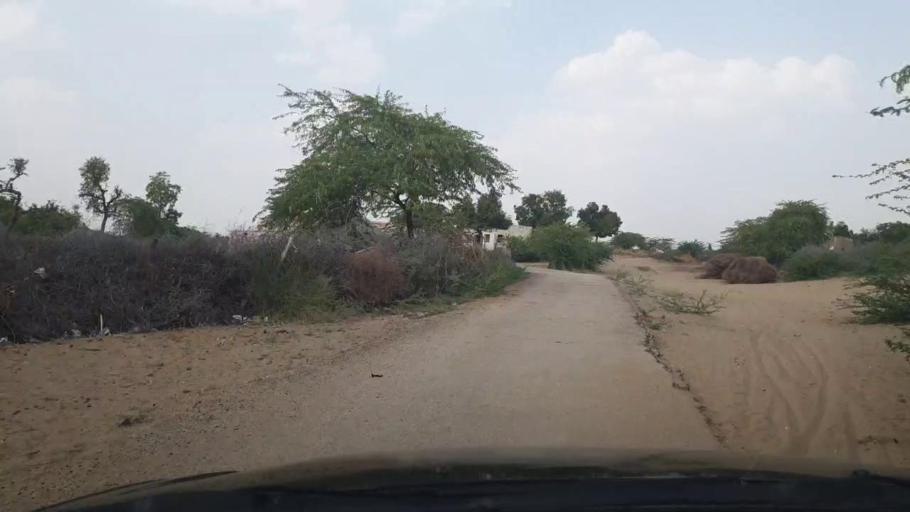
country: PK
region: Sindh
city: Islamkot
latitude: 24.9917
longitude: 70.5776
